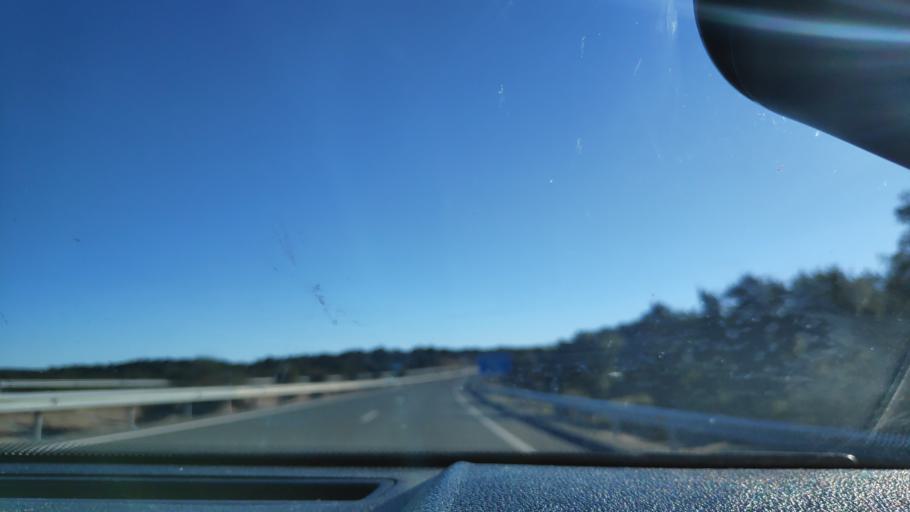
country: ES
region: Andalusia
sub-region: Provincia de Huelva
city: Santa Olalla del Cala
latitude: 37.9406
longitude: -6.2271
